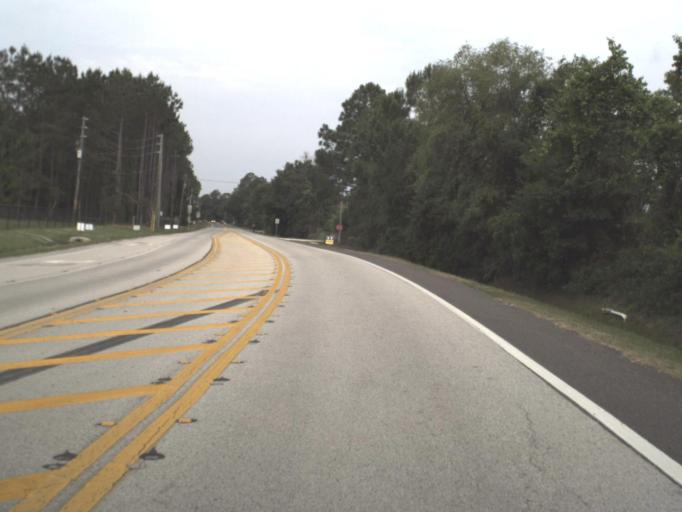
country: US
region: Florida
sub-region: Clay County
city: Green Cove Springs
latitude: 29.9736
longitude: -81.5234
